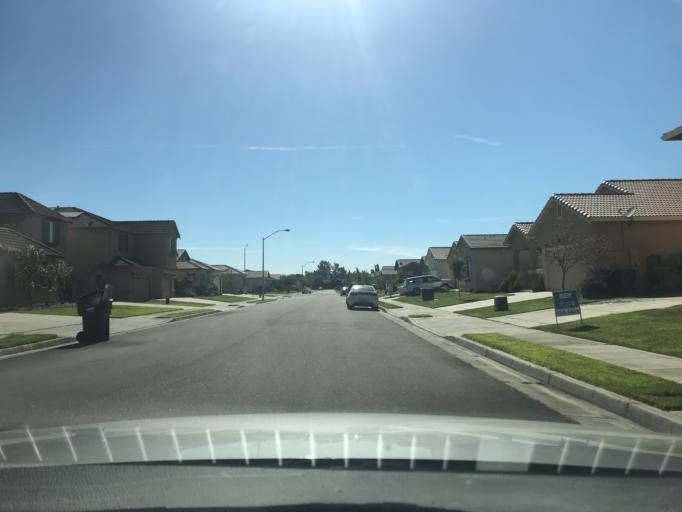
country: US
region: California
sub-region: Merced County
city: Atwater
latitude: 37.3398
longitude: -120.5733
